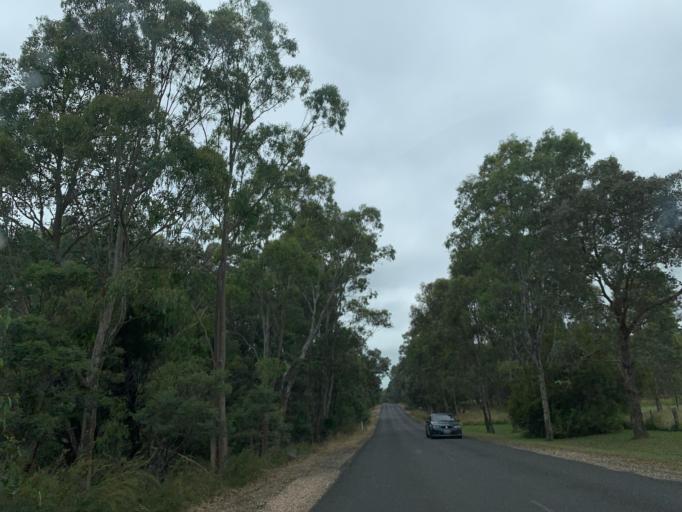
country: AU
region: Victoria
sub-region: Wellington
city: Heyfield
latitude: -37.9344
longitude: 146.7709
